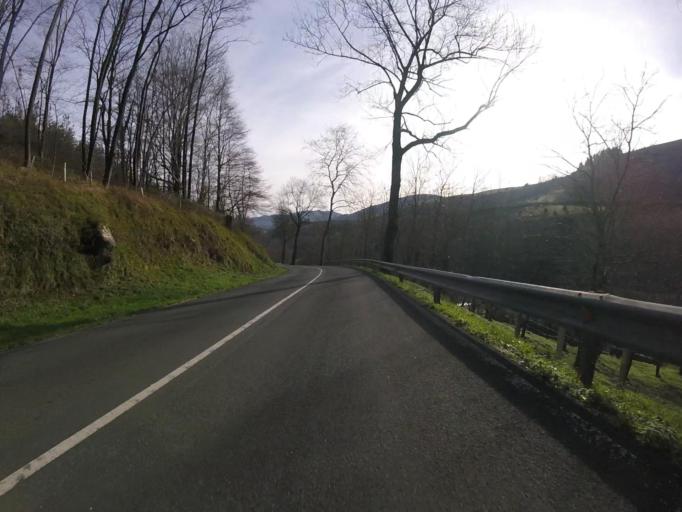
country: ES
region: Navarre
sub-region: Provincia de Navarra
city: Areso
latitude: 43.0980
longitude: -1.9534
